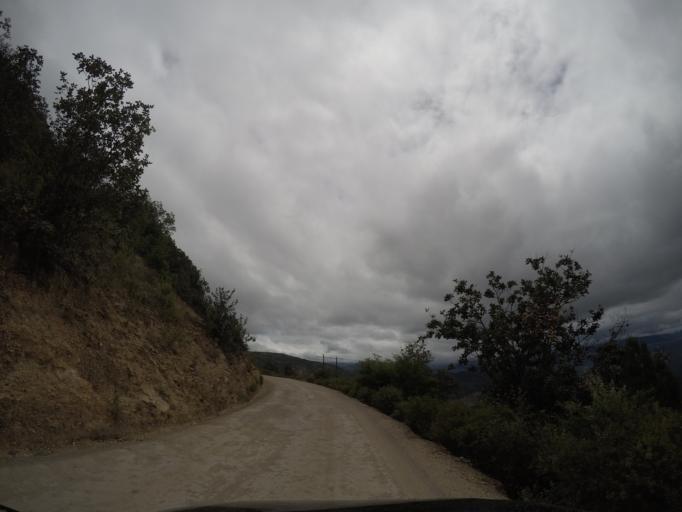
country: MX
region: Oaxaca
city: San Lorenzo Albarradas
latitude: 16.8926
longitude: -96.2626
